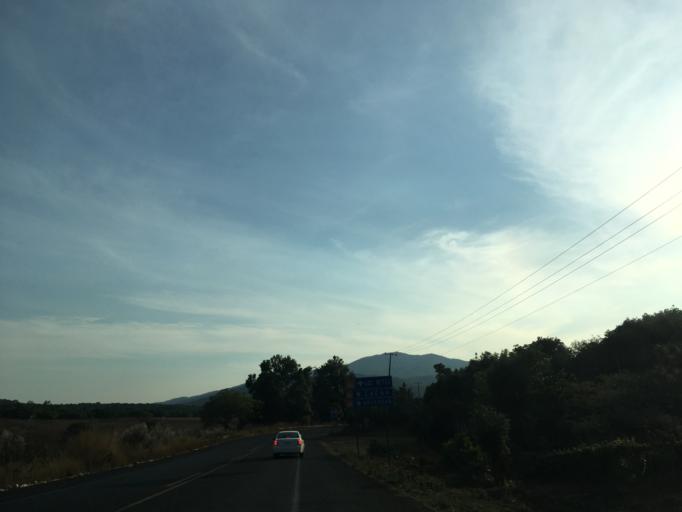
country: MX
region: Michoacan
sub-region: Tingueindin
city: Tingueindin
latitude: 19.7098
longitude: -102.4828
